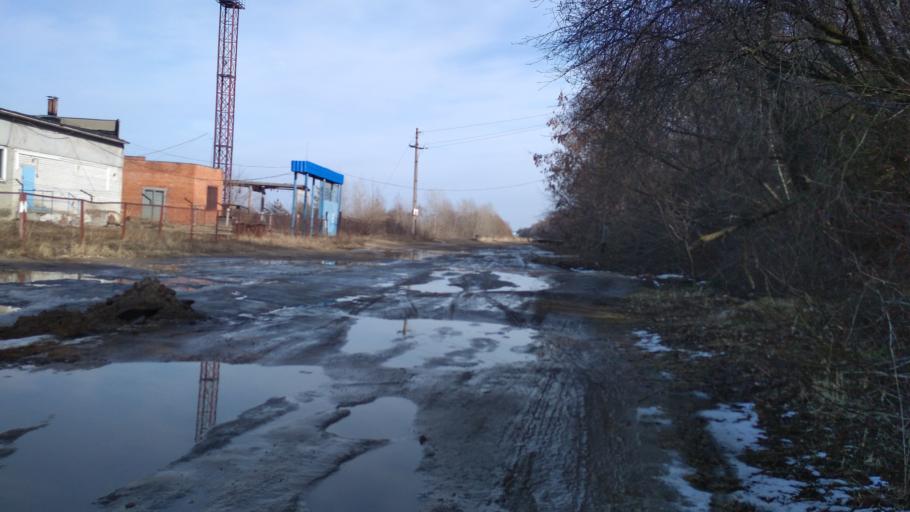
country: RU
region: Chuvashia
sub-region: Cheboksarskiy Rayon
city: Cheboksary
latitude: 56.1471
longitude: 47.3023
